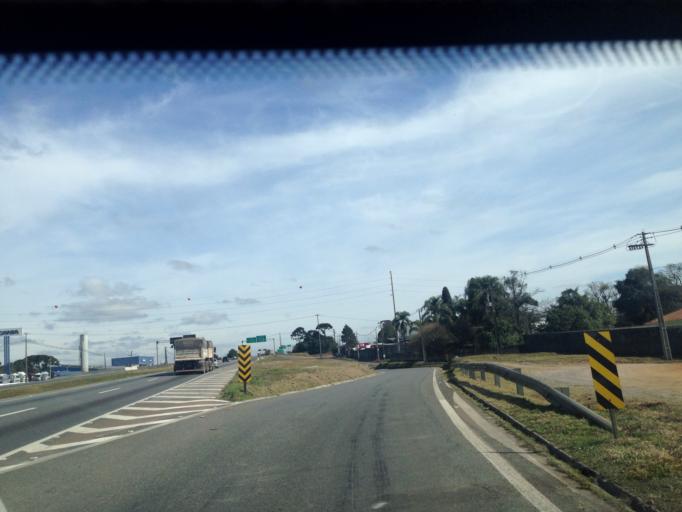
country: BR
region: Parana
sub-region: Sao Jose Dos Pinhais
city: Sao Jose dos Pinhais
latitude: -25.5671
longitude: -49.1717
